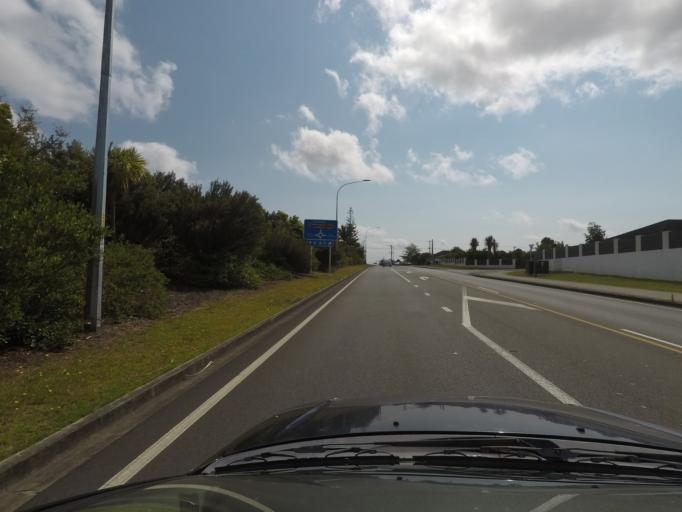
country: NZ
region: Northland
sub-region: Whangarei
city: Whangarei
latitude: -35.6887
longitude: 174.3223
